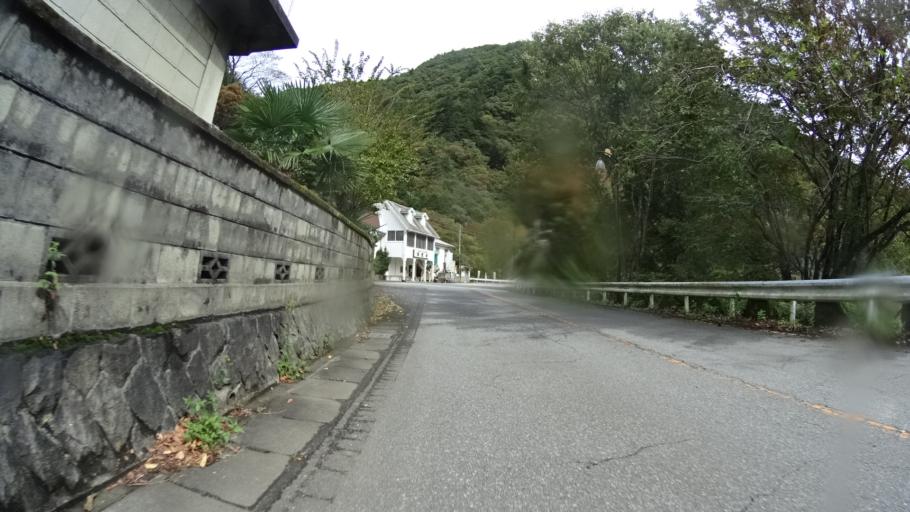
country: JP
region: Yamanashi
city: Otsuki
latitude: 35.7805
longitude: 138.9850
